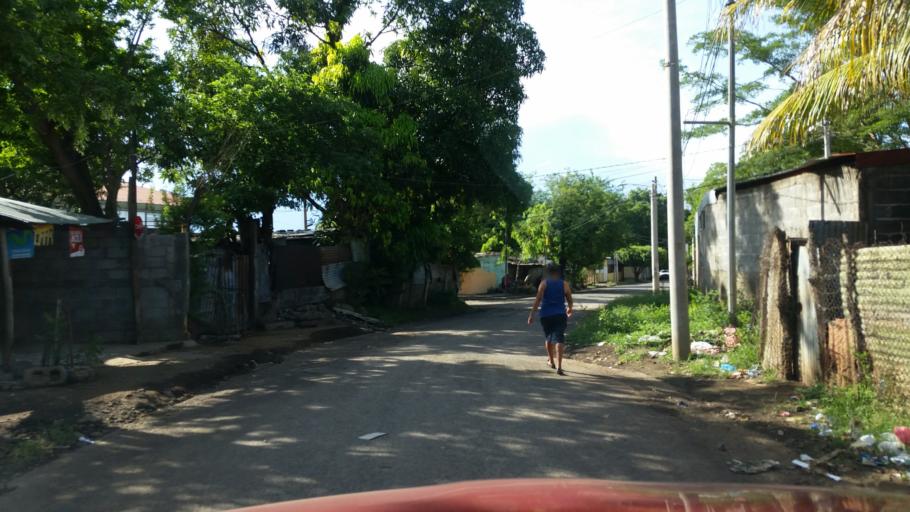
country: NI
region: Managua
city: Managua
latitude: 12.1366
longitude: -86.2649
